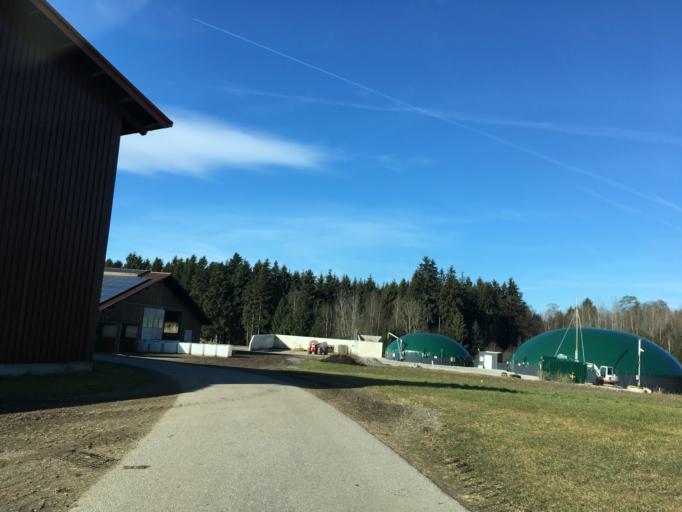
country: DE
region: Bavaria
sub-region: Upper Bavaria
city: Prutting
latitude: 47.9120
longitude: 12.1854
